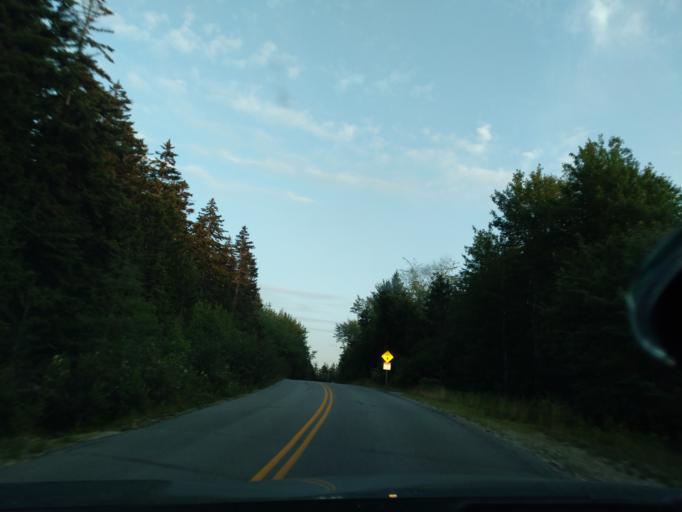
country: US
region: Maine
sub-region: Hancock County
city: Gouldsboro
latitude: 44.3928
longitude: -68.0737
